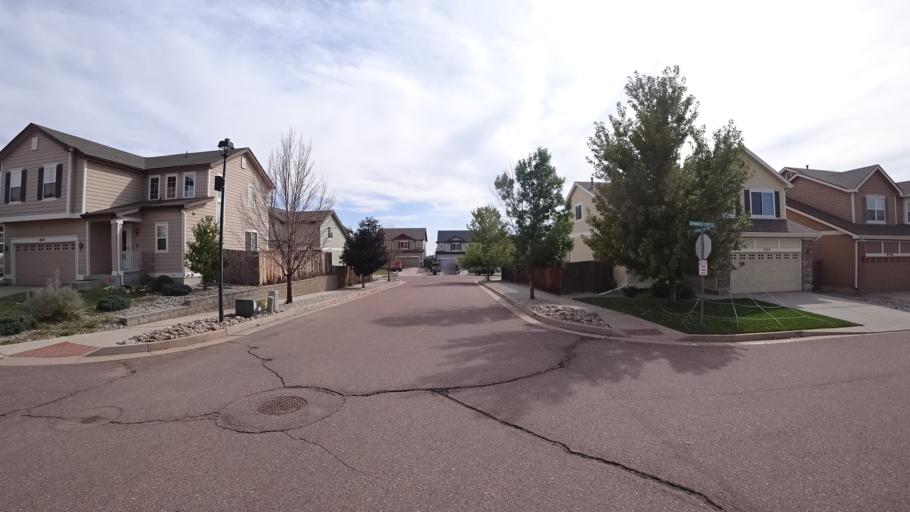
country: US
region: Colorado
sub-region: El Paso County
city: Cimarron Hills
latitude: 38.9034
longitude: -104.6839
